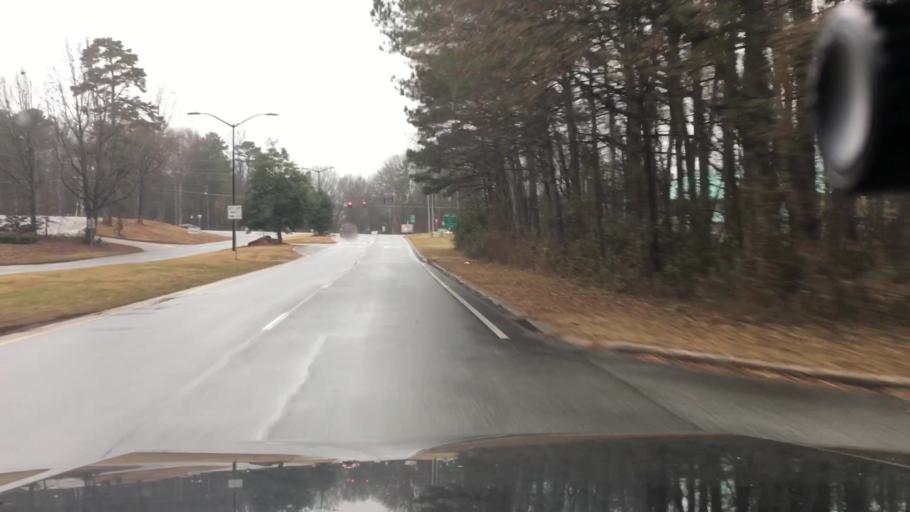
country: US
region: Georgia
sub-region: Coweta County
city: East Newnan
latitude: 33.3976
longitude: -84.7327
